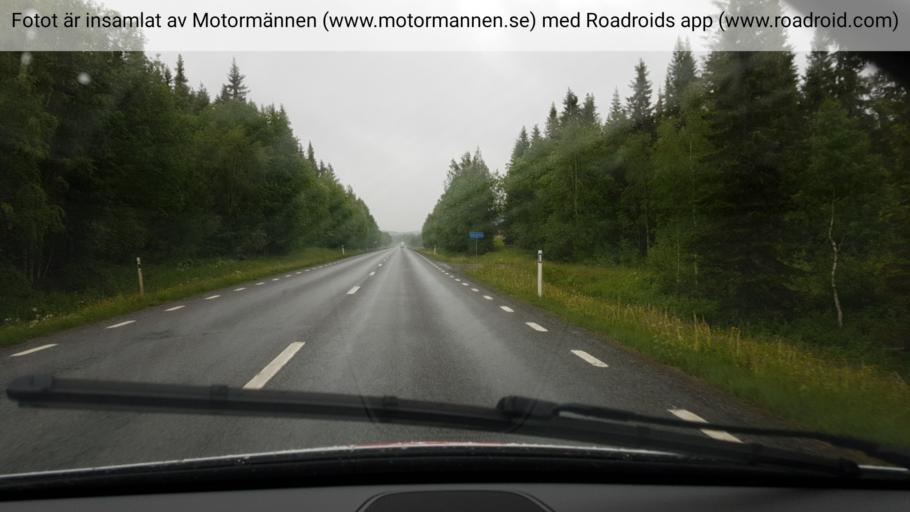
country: SE
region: Jaemtland
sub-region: OEstersunds Kommun
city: Lit
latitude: 63.4223
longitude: 15.1102
